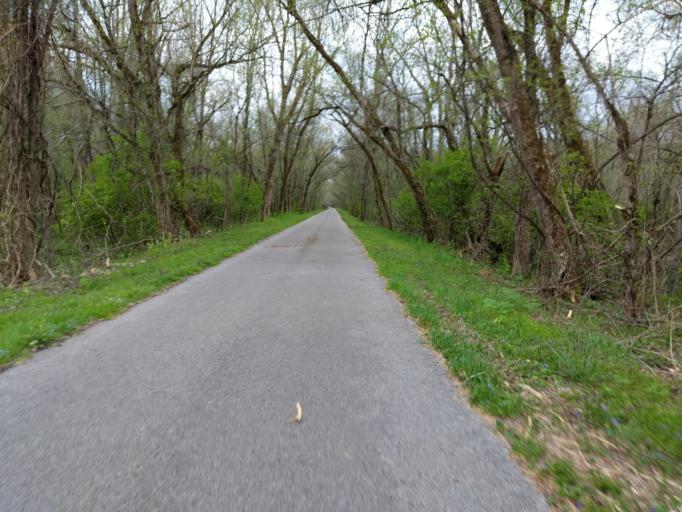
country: US
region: Ohio
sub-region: Athens County
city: The Plains
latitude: 39.3778
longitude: -82.1150
